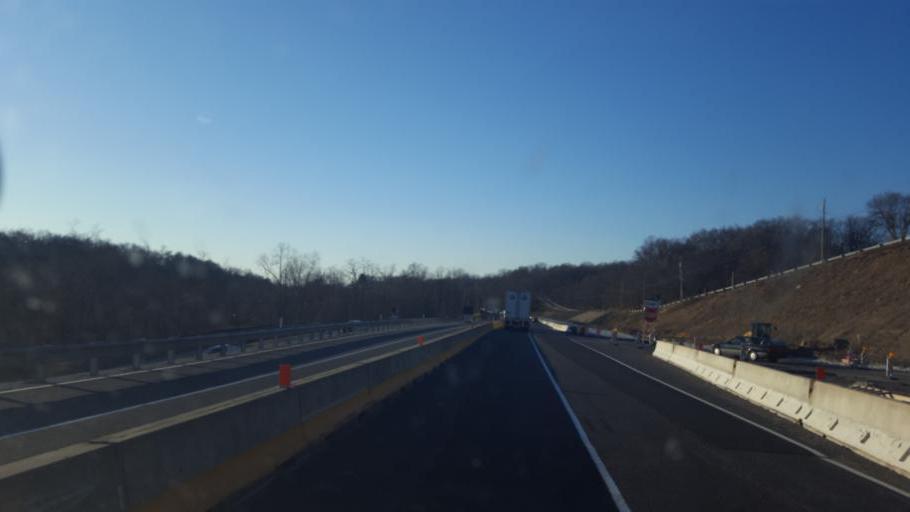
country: US
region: Pennsylvania
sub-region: Washington County
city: Bentleyville
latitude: 40.1255
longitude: -79.9586
